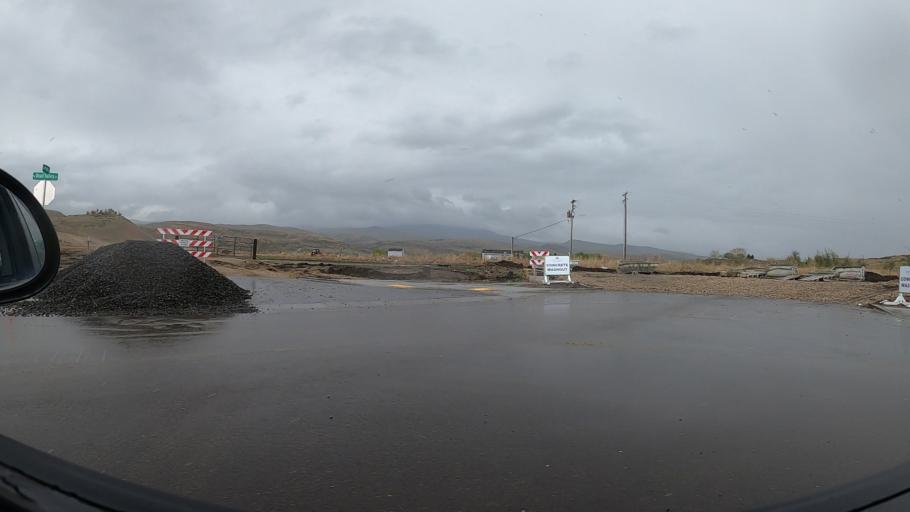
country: US
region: Idaho
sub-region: Ada County
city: Eagle
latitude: 43.7337
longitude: -116.2801
